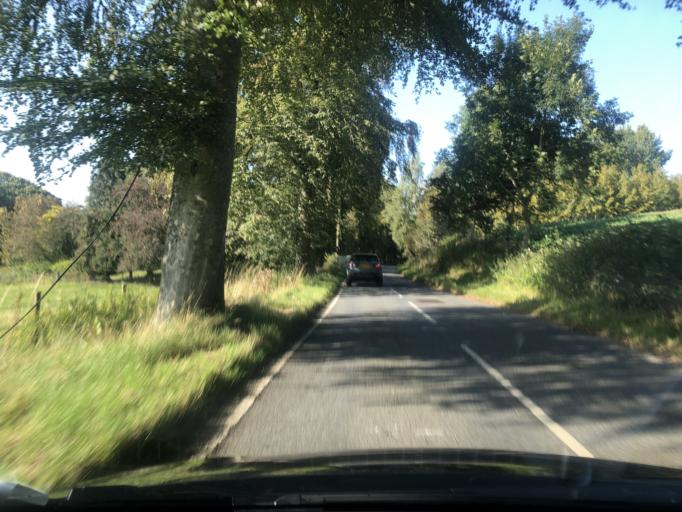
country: GB
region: Scotland
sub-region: Perth and Kinross
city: Blairgowrie
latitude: 56.6877
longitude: -3.4782
